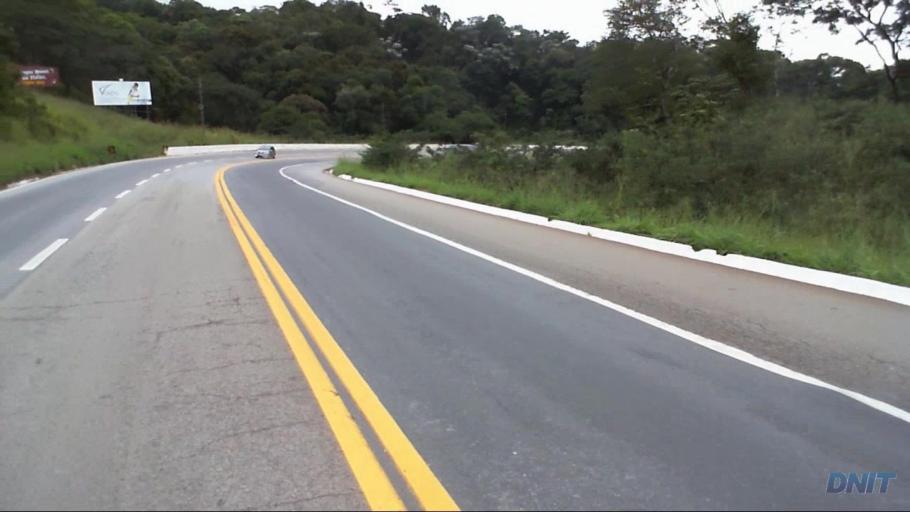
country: BR
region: Minas Gerais
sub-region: Caete
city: Caete
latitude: -19.7370
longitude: -43.5156
